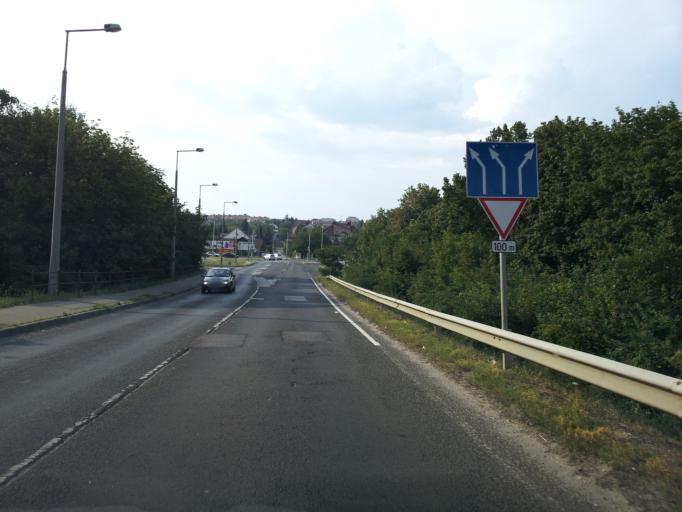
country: HU
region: Budapest
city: Budapest XXII. keruelet
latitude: 47.4094
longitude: 19.0237
